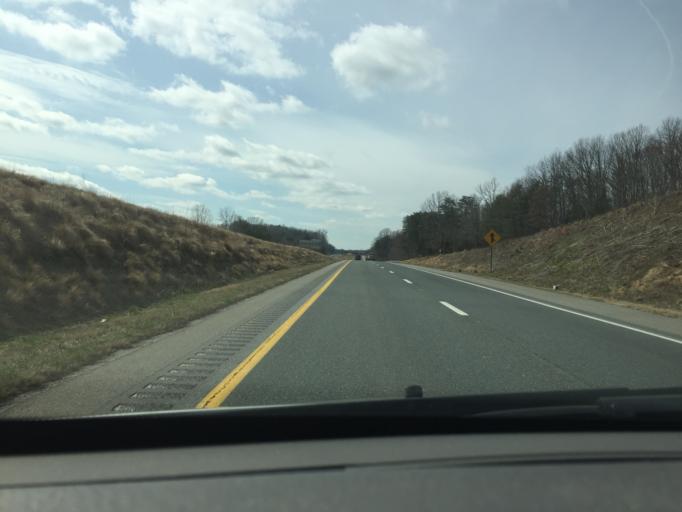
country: US
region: Virginia
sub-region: Campbell County
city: Timberlake
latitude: 37.3309
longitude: -79.2092
